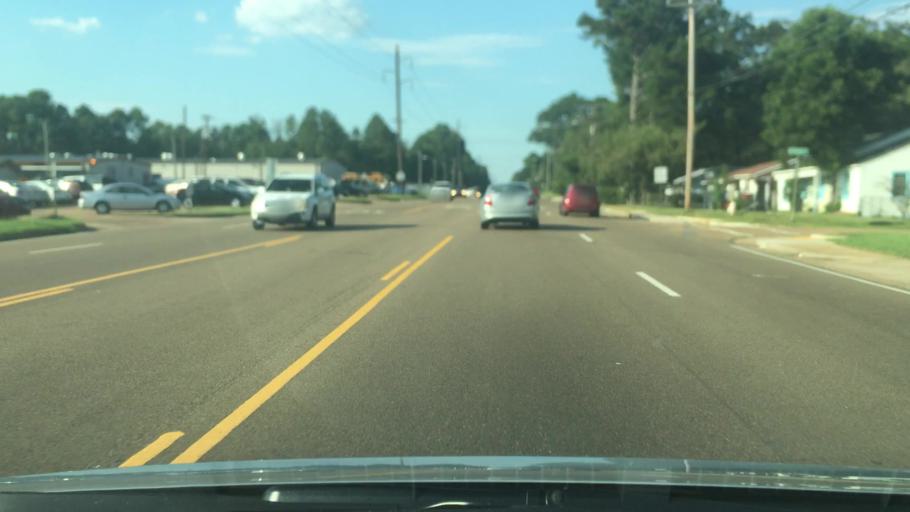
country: US
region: Mississippi
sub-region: Hinds County
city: Jackson
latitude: 32.3580
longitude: -90.1927
